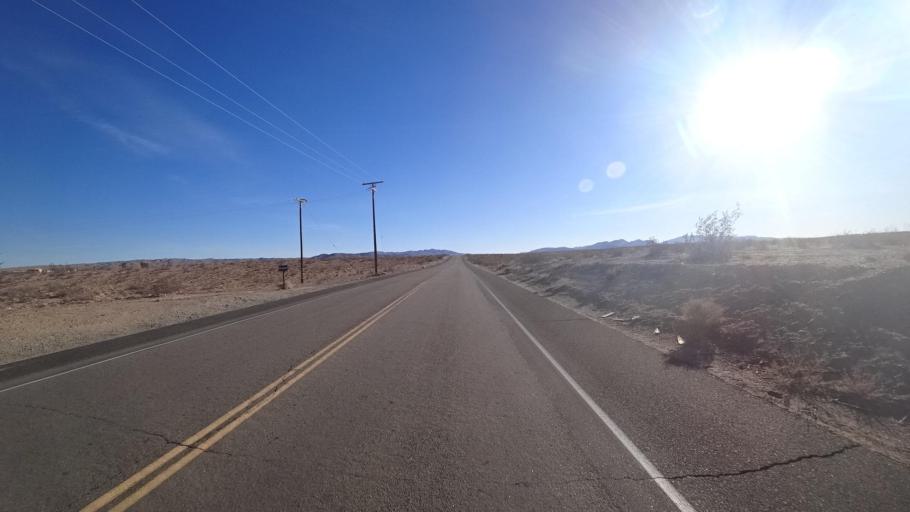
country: US
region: California
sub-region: Kern County
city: China Lake Acres
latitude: 35.6194
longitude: -117.7230
